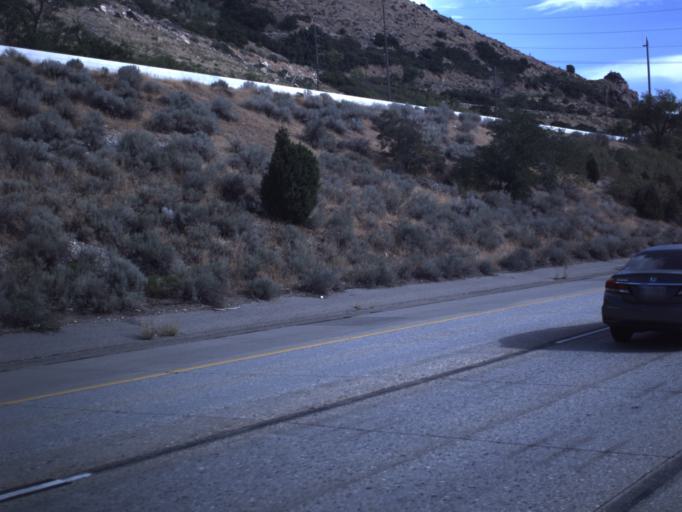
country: US
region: Utah
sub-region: Salt Lake County
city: Holladay
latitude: 40.6582
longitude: -111.8070
